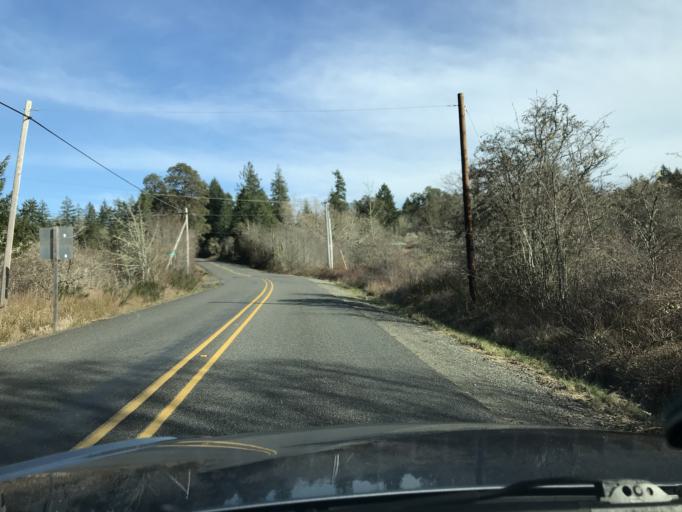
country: US
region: Washington
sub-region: Pierce County
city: Home
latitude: 47.2501
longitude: -122.7529
